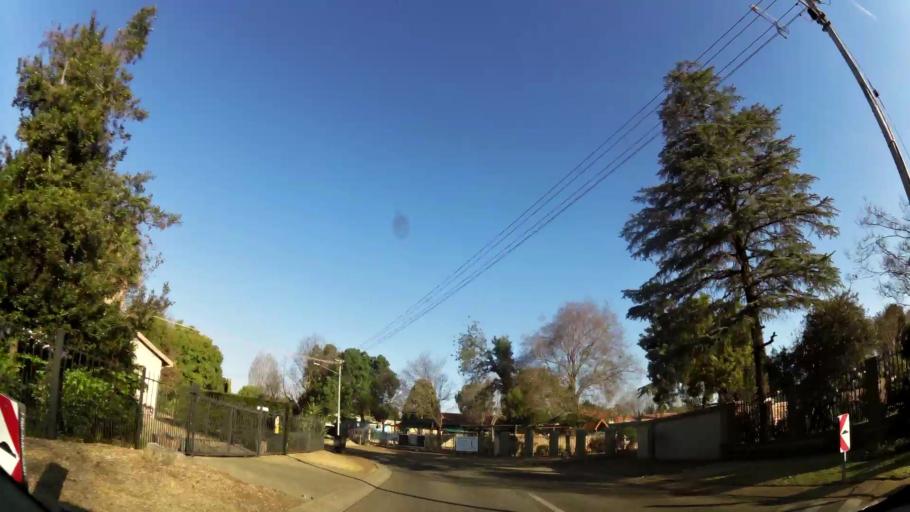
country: ZA
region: Gauteng
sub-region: City of Tshwane Metropolitan Municipality
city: Centurion
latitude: -25.8667
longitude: 28.1397
